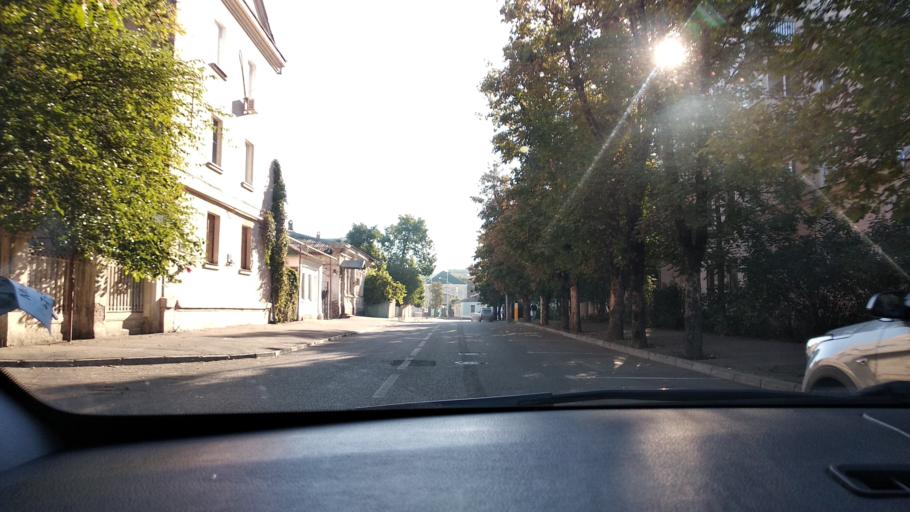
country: RU
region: Krasnodarskiy
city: Krasnodar
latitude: 45.0215
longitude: 38.9743
